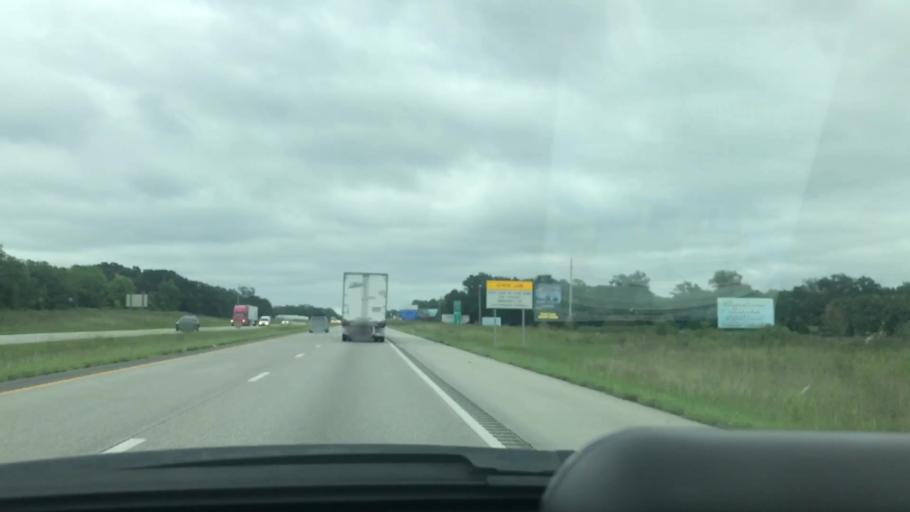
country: US
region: Kansas
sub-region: Cherokee County
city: Galena
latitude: 37.0015
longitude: -94.5943
